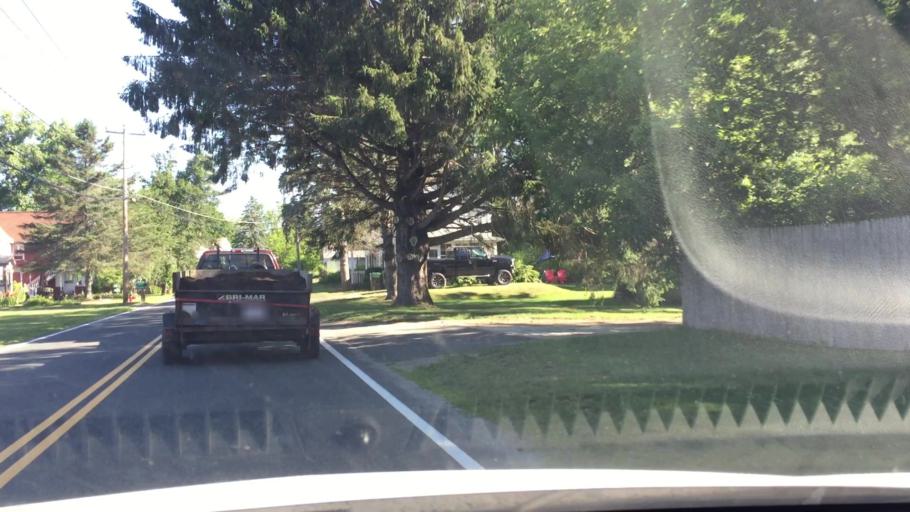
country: US
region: Massachusetts
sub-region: Berkshire County
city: Lee
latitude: 42.2931
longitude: -73.2388
